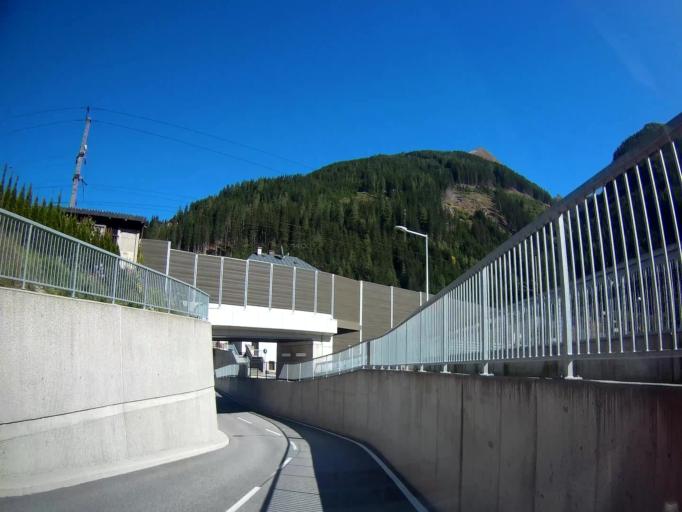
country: AT
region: Salzburg
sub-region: Politischer Bezirk Sankt Johann im Pongau
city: Bad Gastein
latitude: 47.1087
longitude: 13.1332
